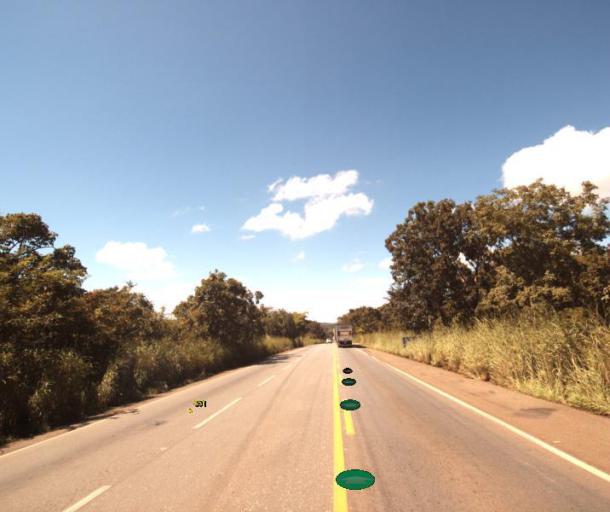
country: BR
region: Goias
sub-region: Jaragua
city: Jaragua
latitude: -15.6656
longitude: -49.3526
